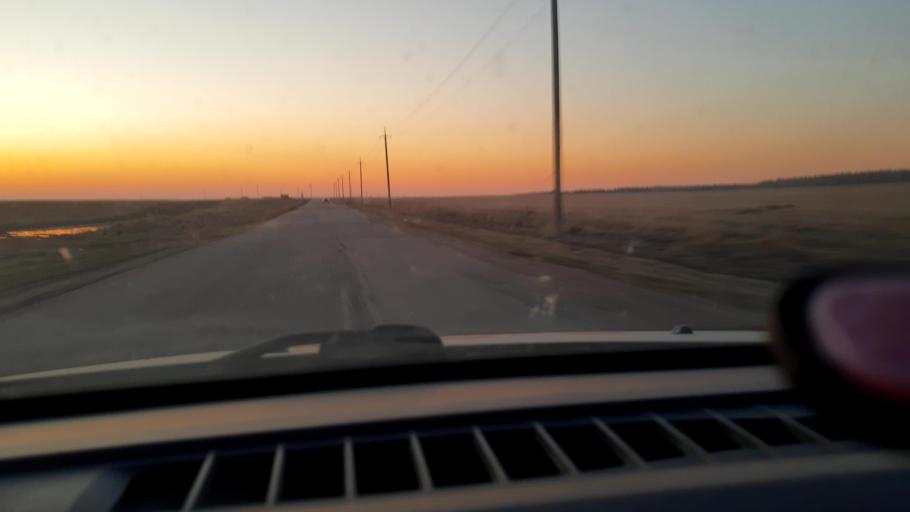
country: RU
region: Bashkortostan
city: Asanovo
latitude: 54.8041
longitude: 55.4899
